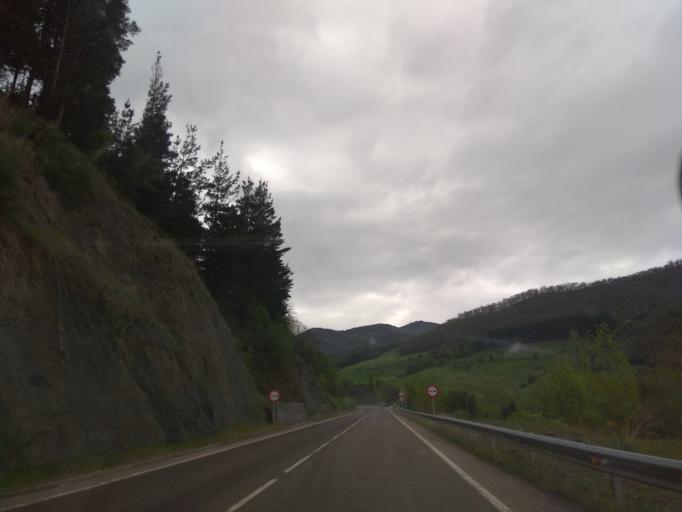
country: ES
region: Cantabria
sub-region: Provincia de Cantabria
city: Potes
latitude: 43.1901
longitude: -4.6043
